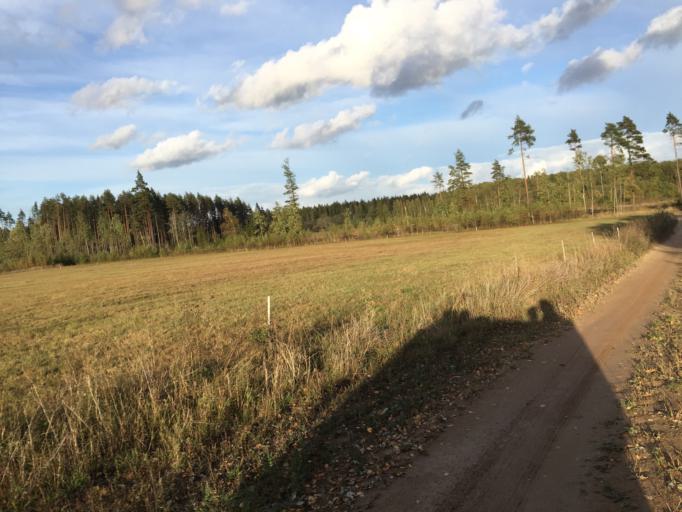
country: LV
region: Malpils
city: Malpils
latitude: 56.9306
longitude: 24.9365
